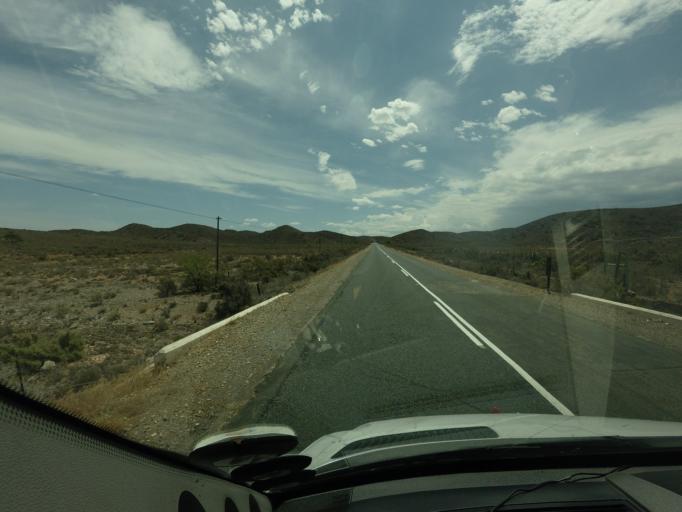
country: ZA
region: Western Cape
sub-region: Eden District Municipality
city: Ladismith
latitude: -33.7077
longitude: 20.9700
